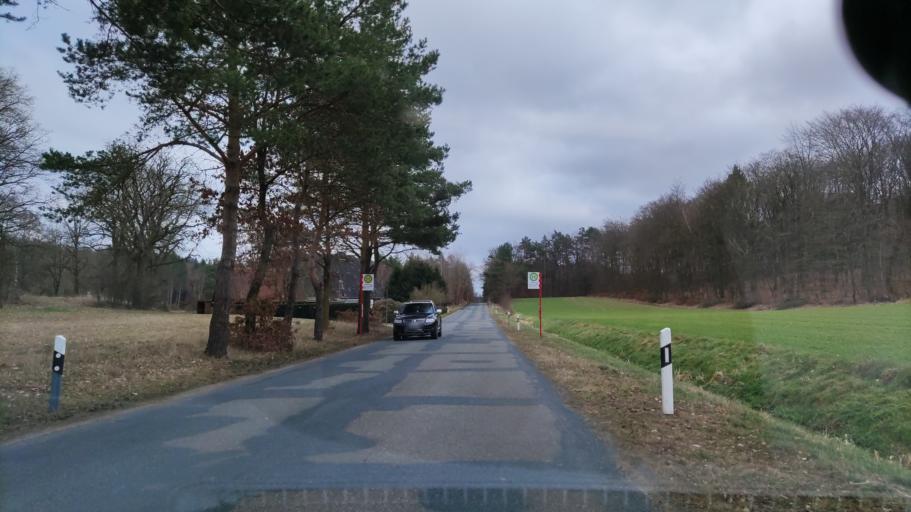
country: DE
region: Lower Saxony
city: Bleckede
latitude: 53.2667
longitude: 10.7182
